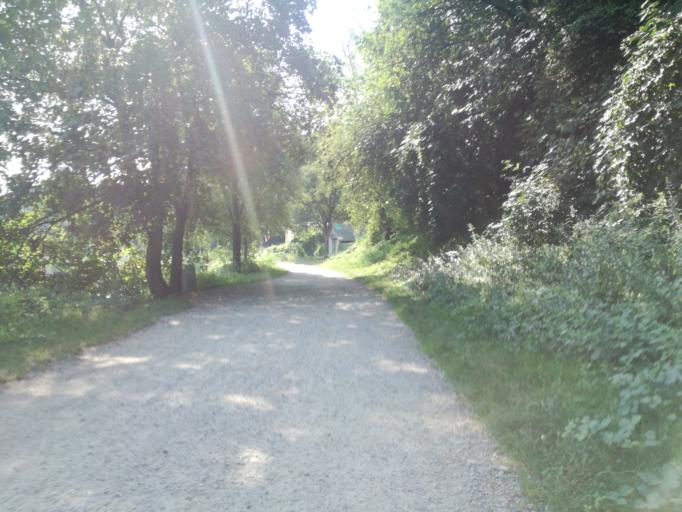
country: IT
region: Lombardy
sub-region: Citta metropolitana di Milano
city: Trezzo sull'Adda
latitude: 45.6128
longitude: 9.5171
